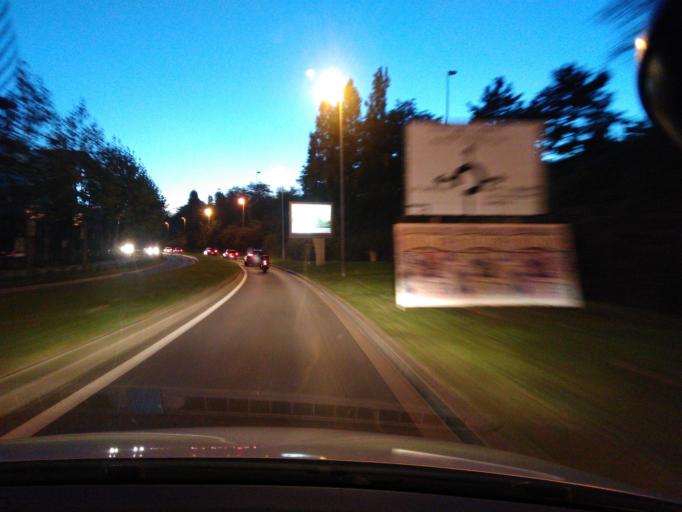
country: FR
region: Ile-de-France
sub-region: Departement du Val-de-Marne
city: Villiers-sur-Marne
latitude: 48.8354
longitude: 2.5407
